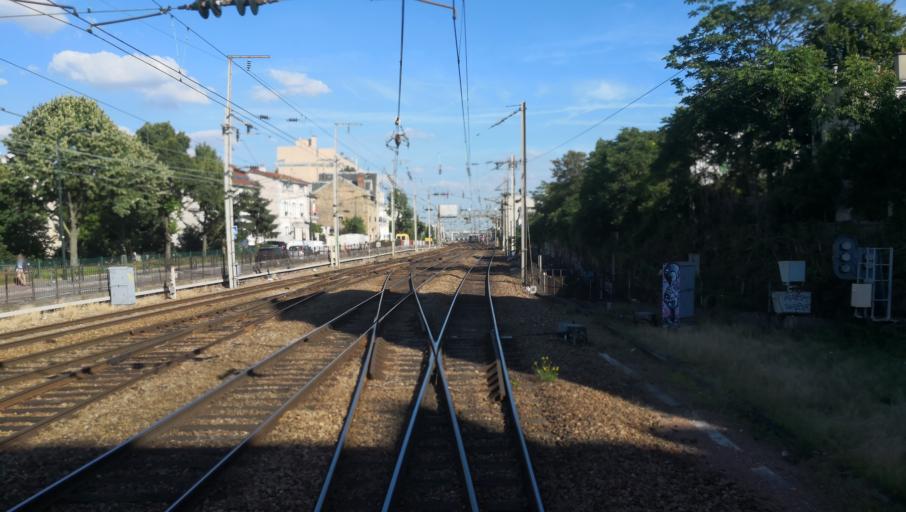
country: FR
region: Ile-de-France
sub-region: Departement des Hauts-de-Seine
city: Asnieres-sur-Seine
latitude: 48.9090
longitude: 2.2786
